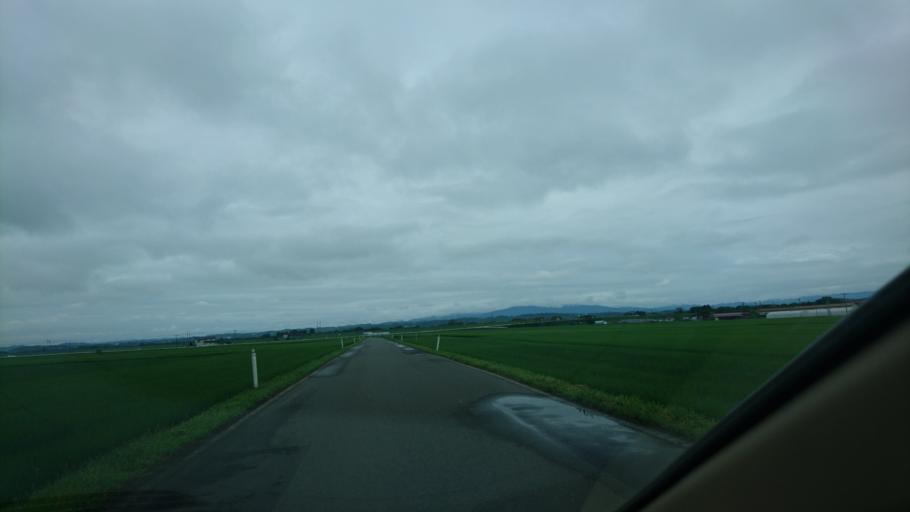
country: JP
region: Iwate
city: Mizusawa
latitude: 39.0635
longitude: 141.1742
